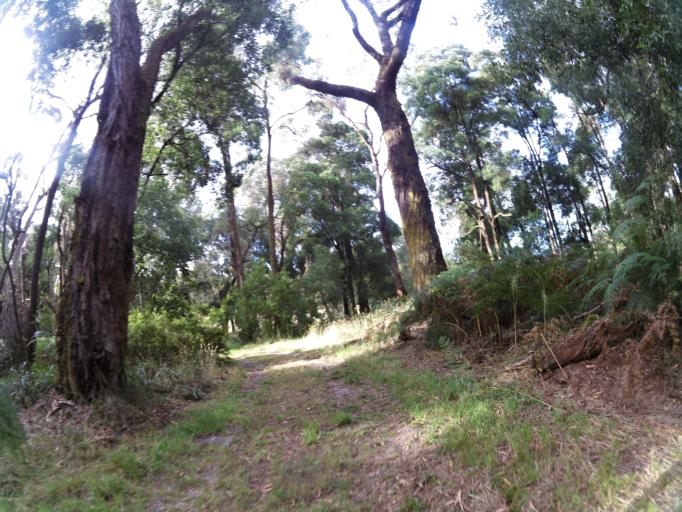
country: AU
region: Victoria
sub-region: Colac-Otway
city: Colac
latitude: -38.5026
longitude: 143.7265
